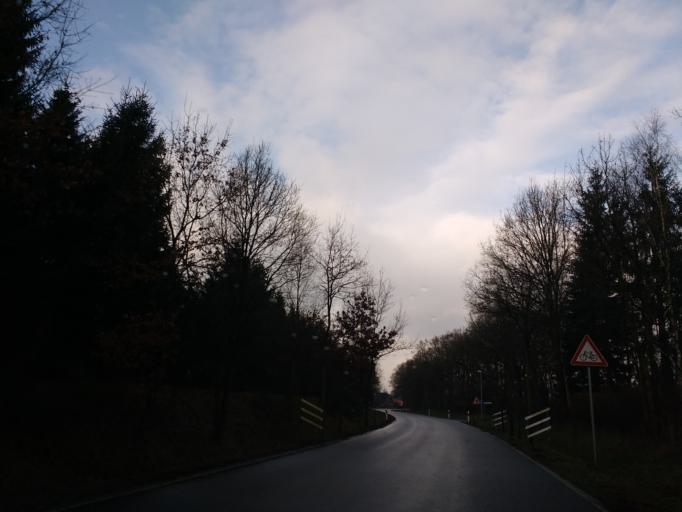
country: DE
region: Schleswig-Holstein
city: Luhnstedt
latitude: 54.2066
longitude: 9.7115
